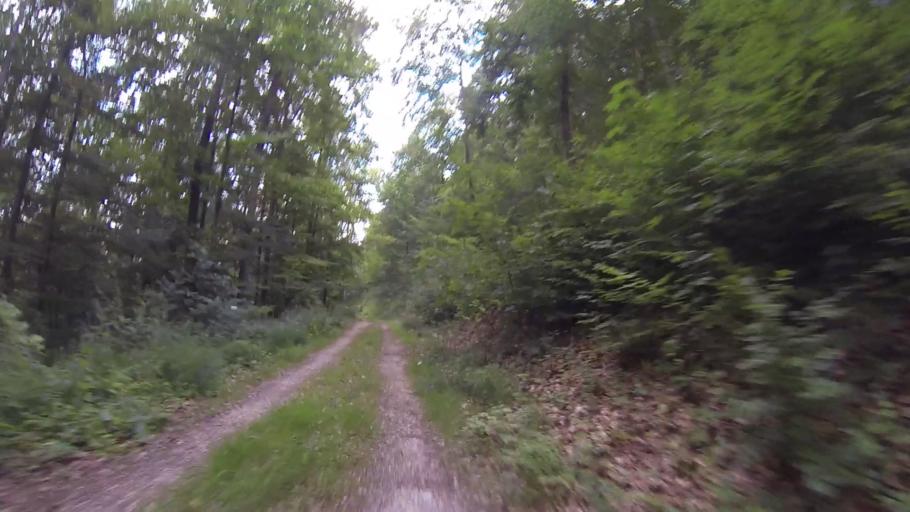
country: DE
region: Baden-Wuerttemberg
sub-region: Tuebingen Region
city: Dornstadt
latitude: 48.4397
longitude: 9.8746
